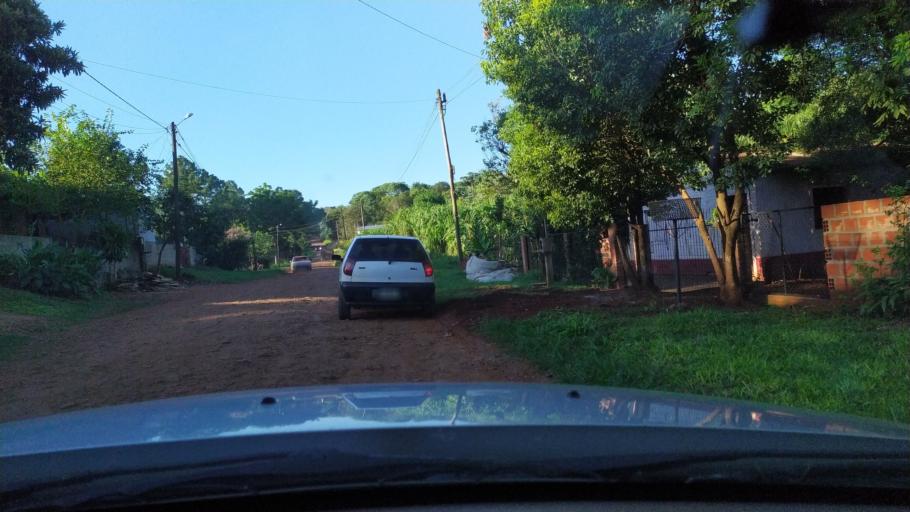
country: AR
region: Misiones
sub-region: Departamento de Eldorado
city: Eldorado
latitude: -26.4139
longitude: -54.6251
